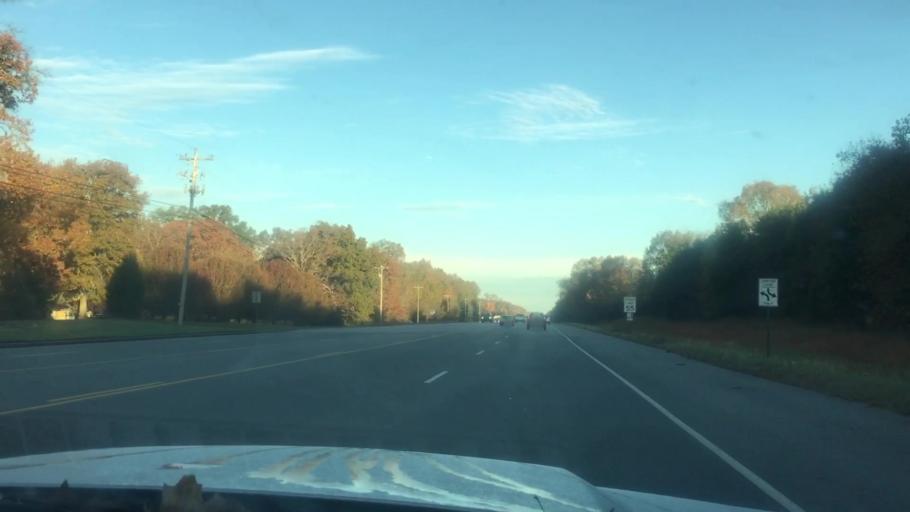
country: US
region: Tennessee
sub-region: Franklin County
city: Estill Springs
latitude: 35.2937
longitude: -86.1481
